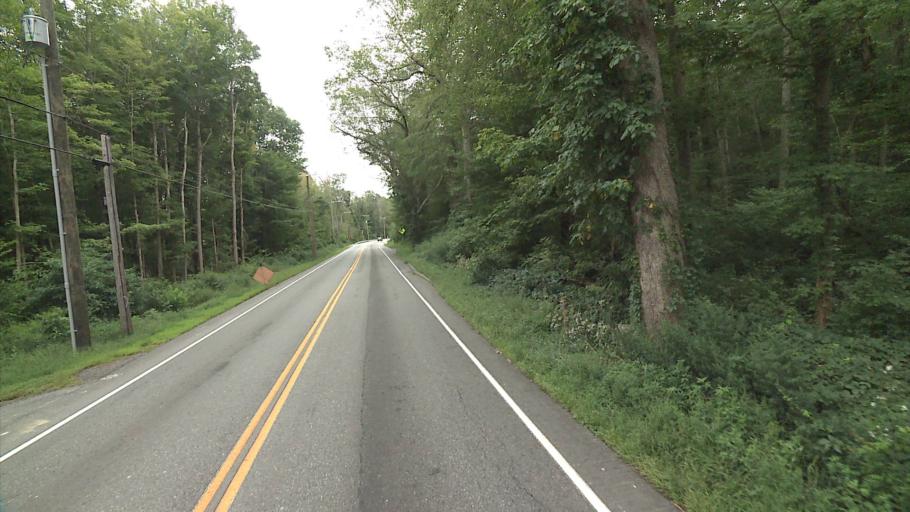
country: US
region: Connecticut
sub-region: New London County
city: Montville Center
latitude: 41.4540
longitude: -72.2391
